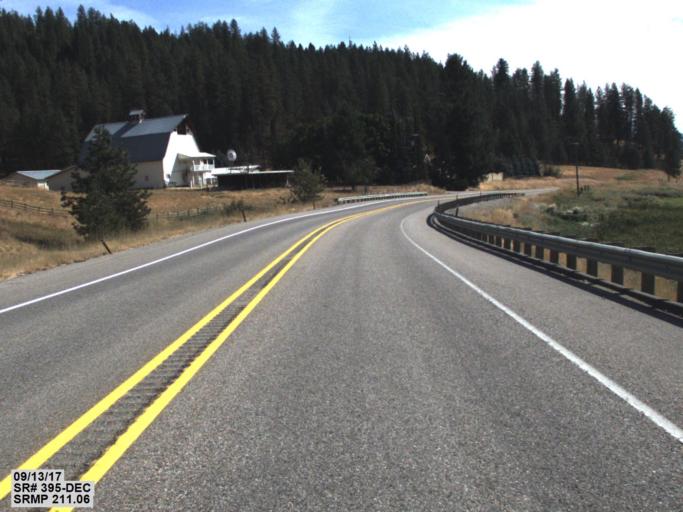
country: US
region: Washington
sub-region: Stevens County
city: Chewelah
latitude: 48.3072
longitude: -117.7799
